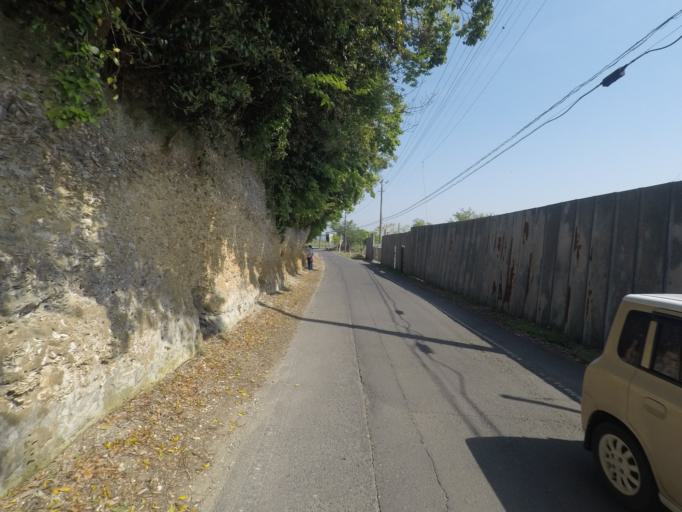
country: JP
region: Ibaraki
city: Ami
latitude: 36.0631
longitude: 140.2904
